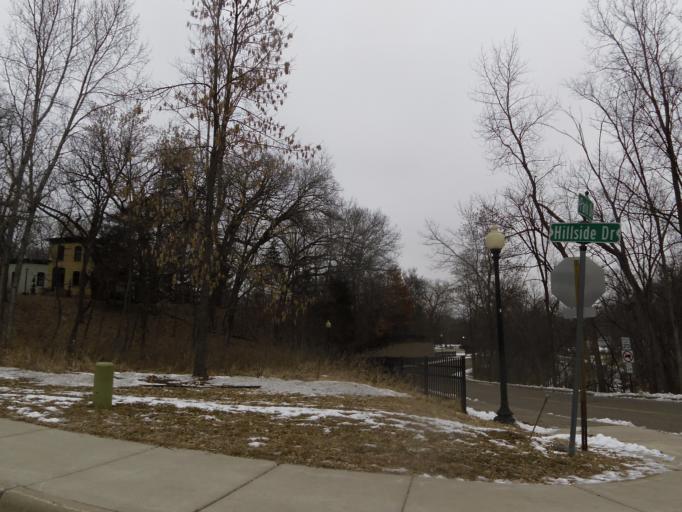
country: US
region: Minnesota
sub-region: Scott County
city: Jordan
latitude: 44.6582
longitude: -93.6306
